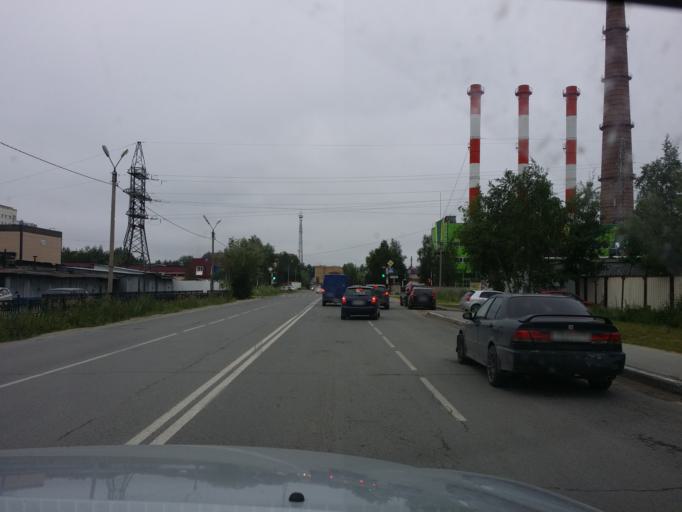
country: RU
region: Khanty-Mansiyskiy Avtonomnyy Okrug
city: Nizhnevartovsk
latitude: 60.9344
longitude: 76.5490
